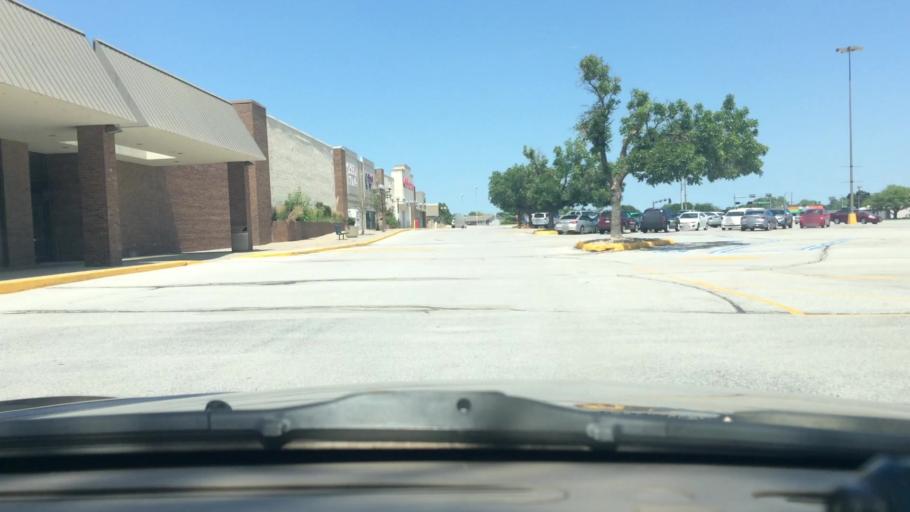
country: US
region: Nebraska
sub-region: Sarpy County
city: La Vista
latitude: 41.1780
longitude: -96.0452
